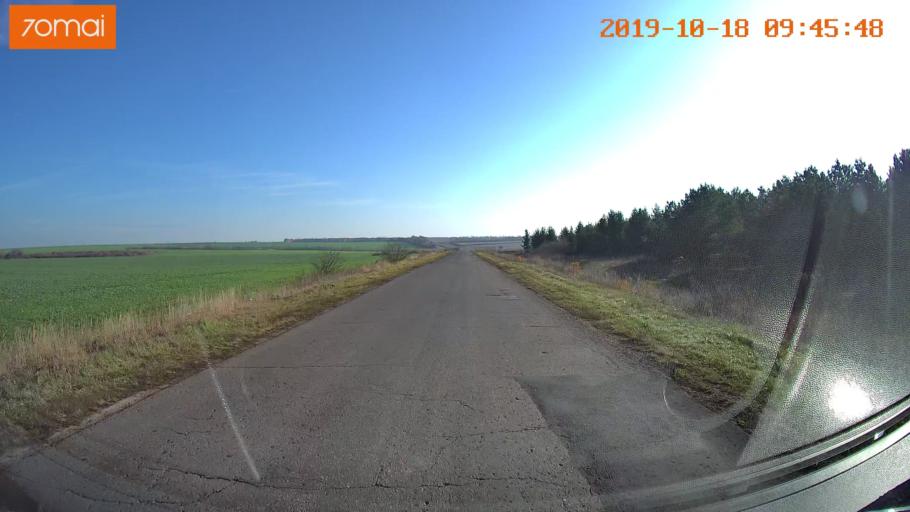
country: RU
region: Tula
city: Kazachka
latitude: 53.3124
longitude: 38.1978
